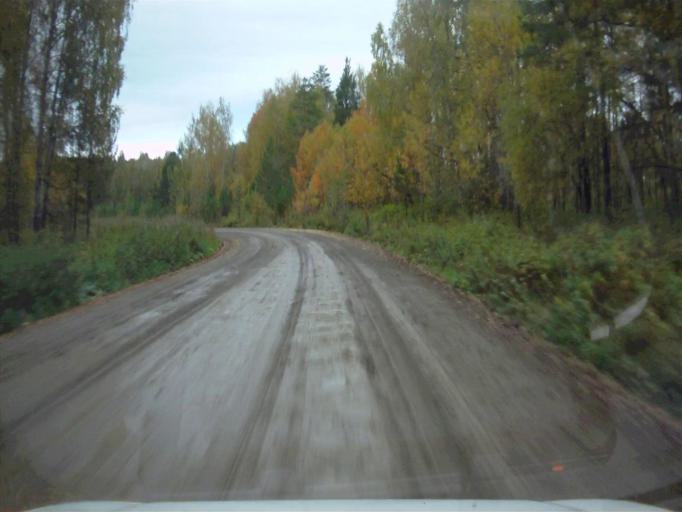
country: RU
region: Chelyabinsk
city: Nyazepetrovsk
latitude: 56.1199
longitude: 59.3697
